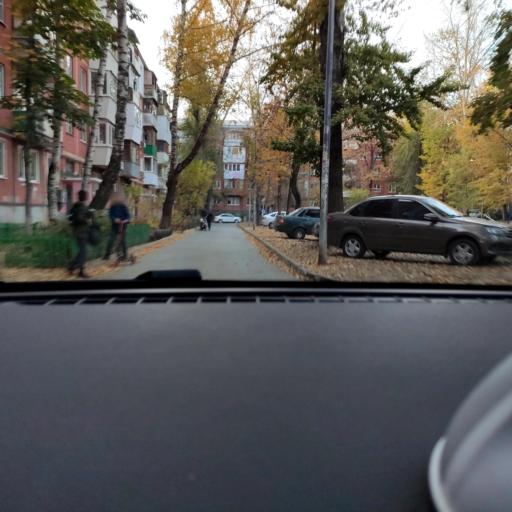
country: RU
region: Samara
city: Samara
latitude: 53.2427
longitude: 50.2456
